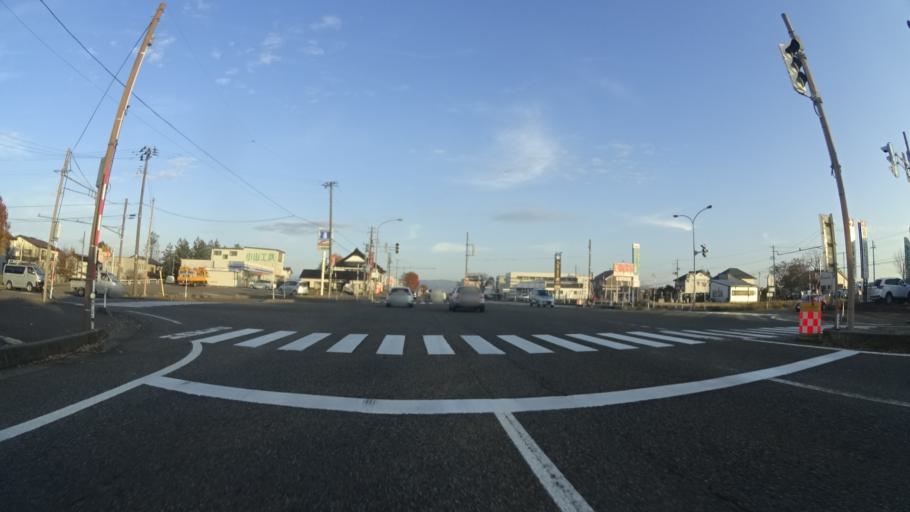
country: JP
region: Niigata
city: Nagaoka
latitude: 37.4485
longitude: 138.7695
